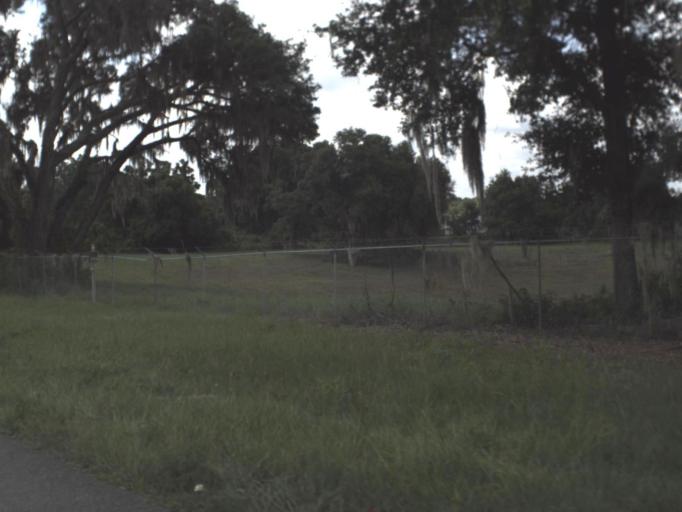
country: US
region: Florida
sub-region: Citrus County
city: Hernando
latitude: 28.9483
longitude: -82.4060
